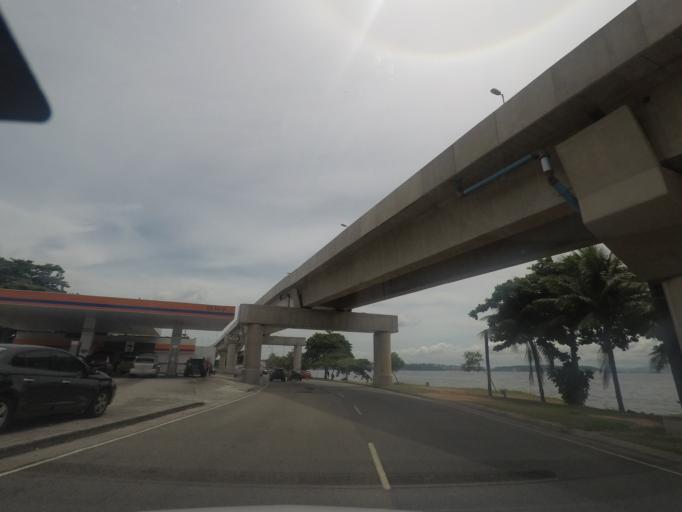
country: BR
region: Rio de Janeiro
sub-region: Rio De Janeiro
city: Rio de Janeiro
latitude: -22.8267
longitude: -43.2336
